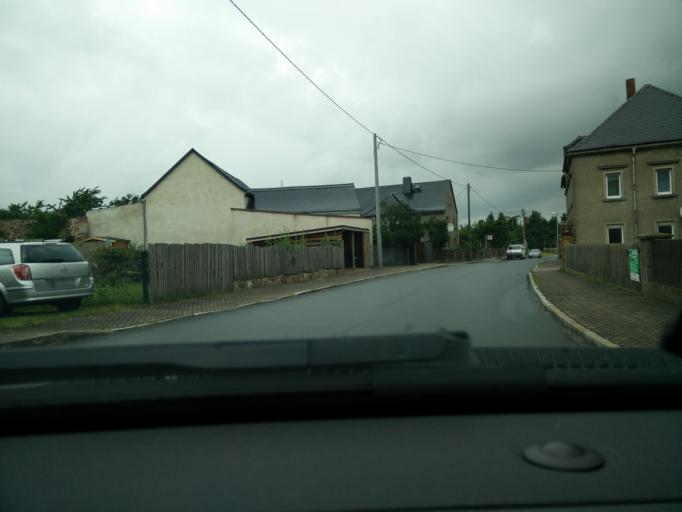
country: DE
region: Saxony
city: Bad Lausick
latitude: 51.1389
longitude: 12.6879
